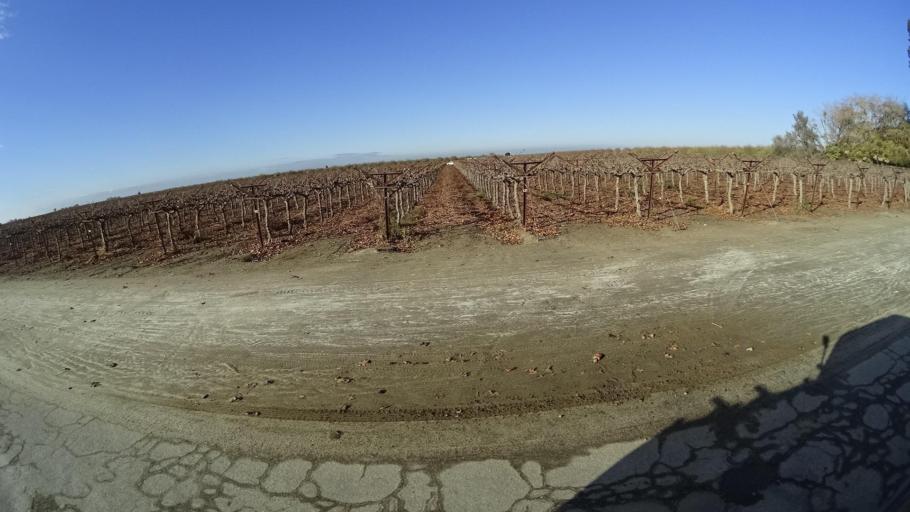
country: US
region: California
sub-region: Kern County
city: Delano
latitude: 35.7315
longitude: -119.3030
